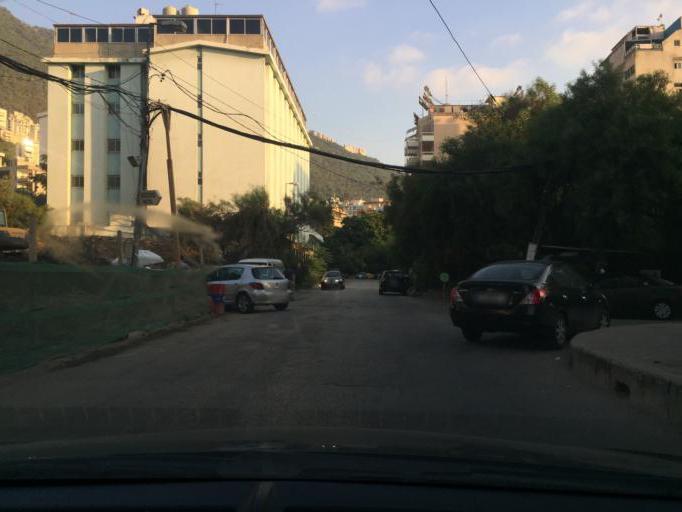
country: LB
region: Mont-Liban
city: Djounie
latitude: 33.9920
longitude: 35.6423
